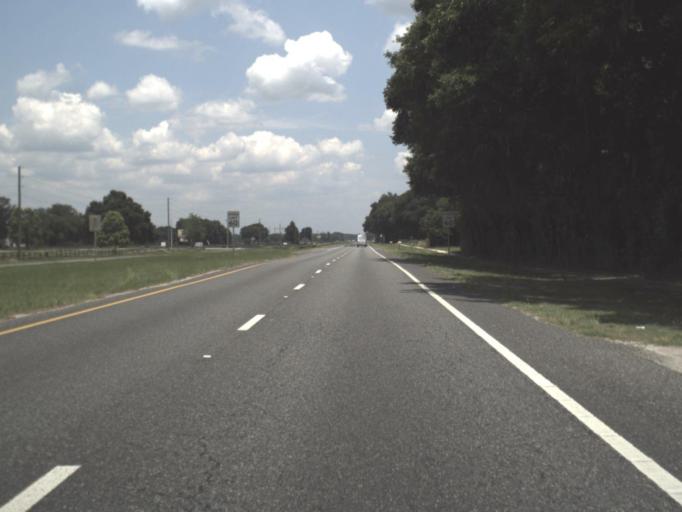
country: US
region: Florida
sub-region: Alachua County
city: Newberry
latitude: 29.6542
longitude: -82.5901
